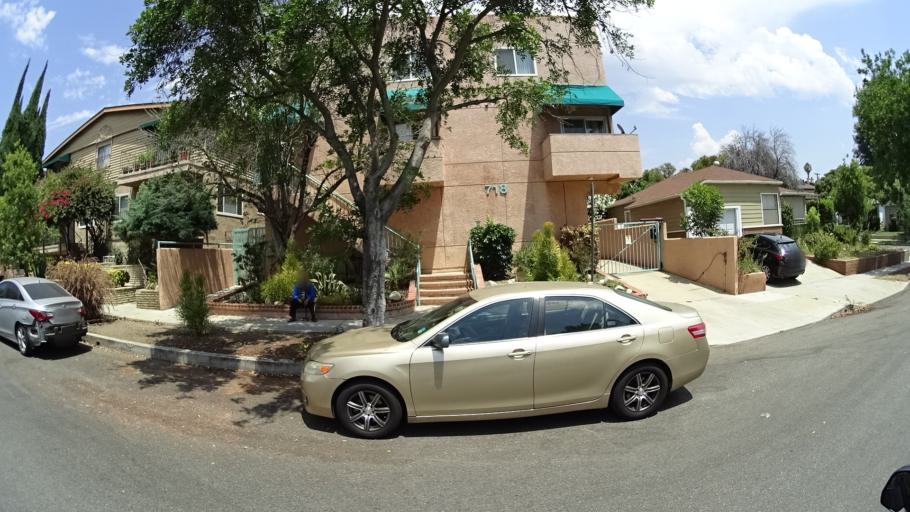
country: US
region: California
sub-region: Los Angeles County
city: Burbank
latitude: 34.1797
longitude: -118.2983
